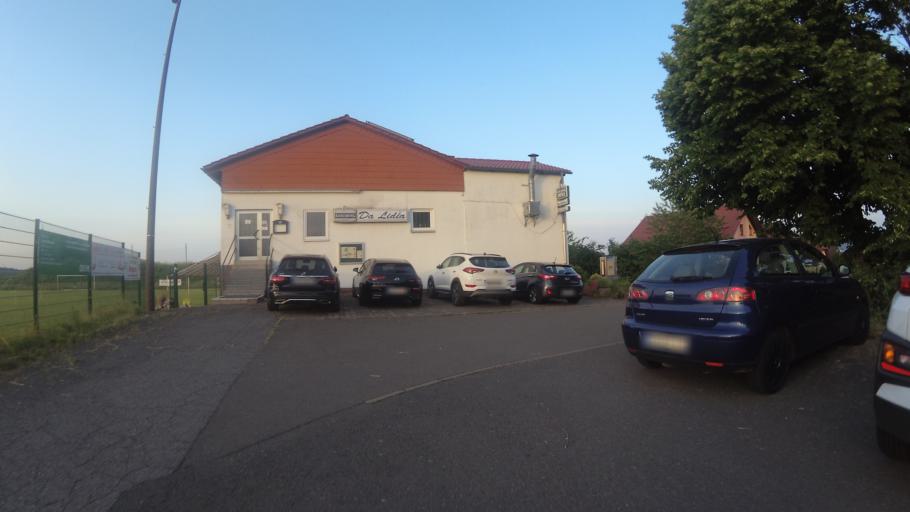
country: DE
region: Rheinland-Pfalz
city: Gries
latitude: 49.4218
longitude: 7.4021
